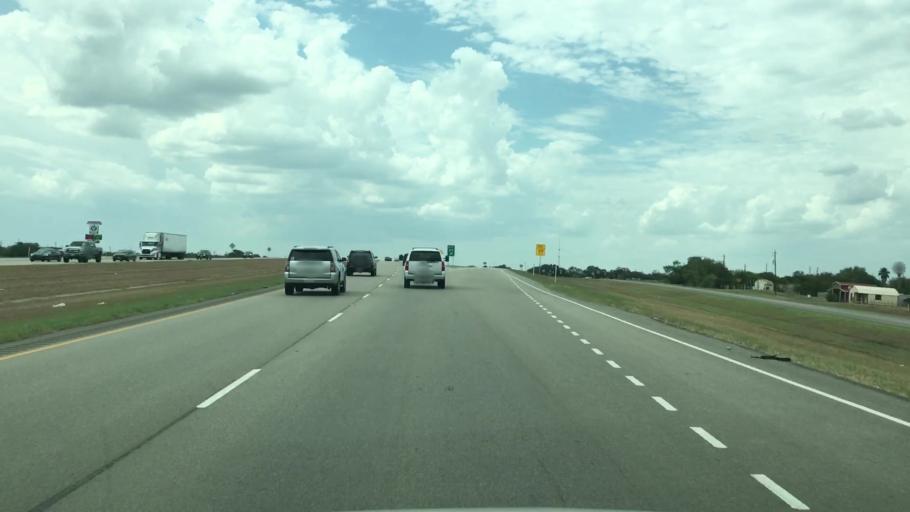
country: US
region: Texas
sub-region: Live Oak County
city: Three Rivers
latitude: 28.4860
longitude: -98.1380
